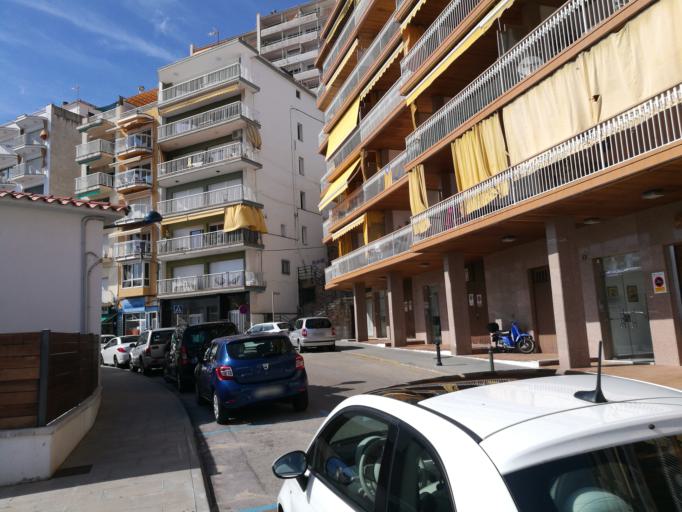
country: ES
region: Catalonia
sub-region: Provincia de Girona
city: Blanes
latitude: 41.6762
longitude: 2.7992
